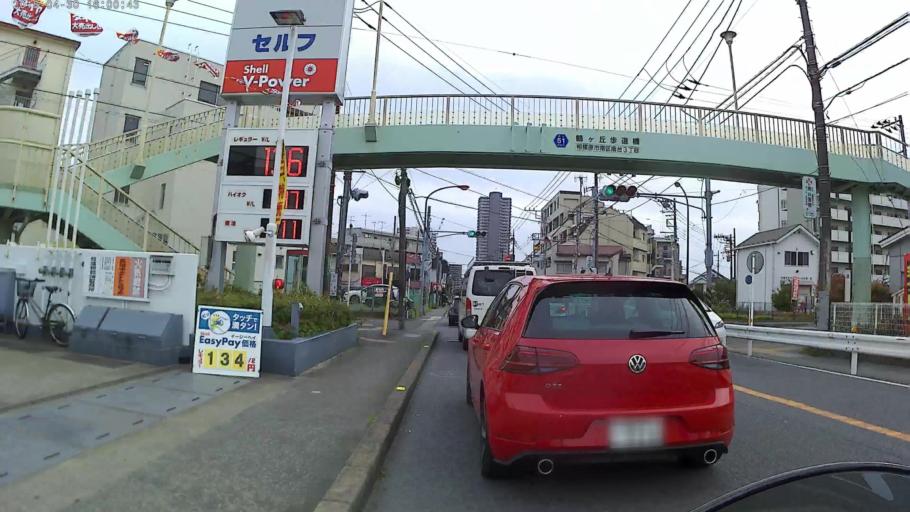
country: JP
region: Tokyo
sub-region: Machida-shi
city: Machida
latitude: 35.5204
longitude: 139.4240
